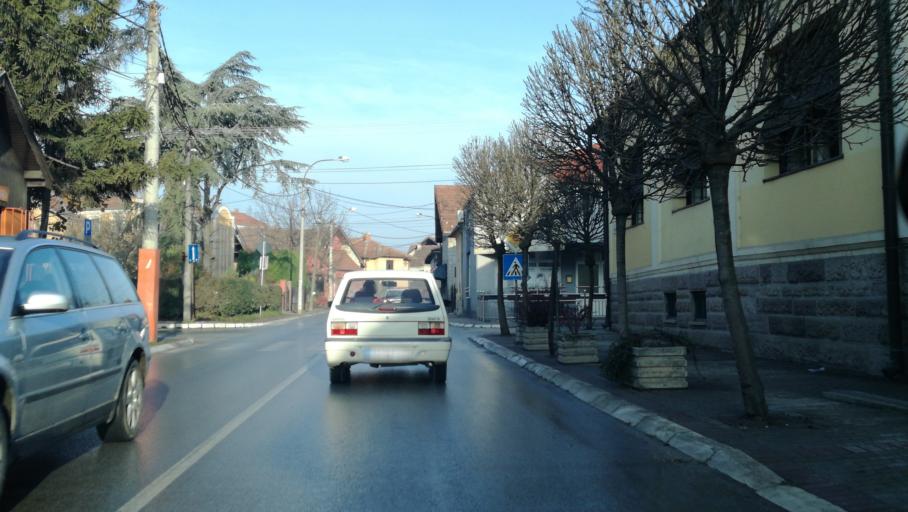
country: RS
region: Central Serbia
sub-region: Moravicki Okrug
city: Cacak
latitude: 43.8920
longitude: 20.3527
